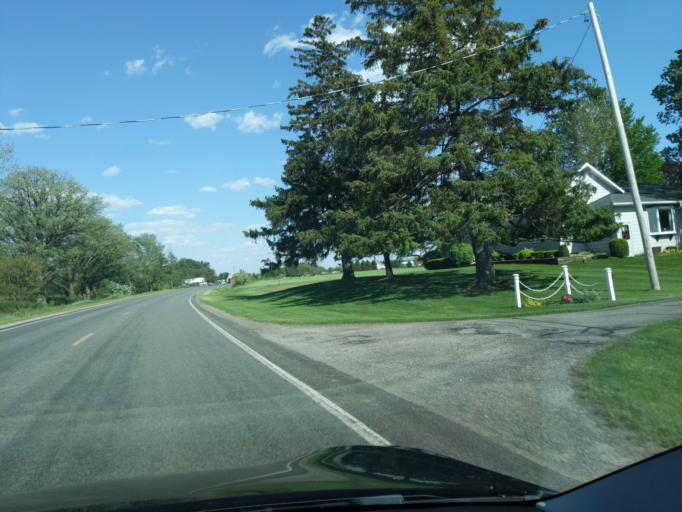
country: US
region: Michigan
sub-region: Ionia County
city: Lake Odessa
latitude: 42.7846
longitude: -85.1646
